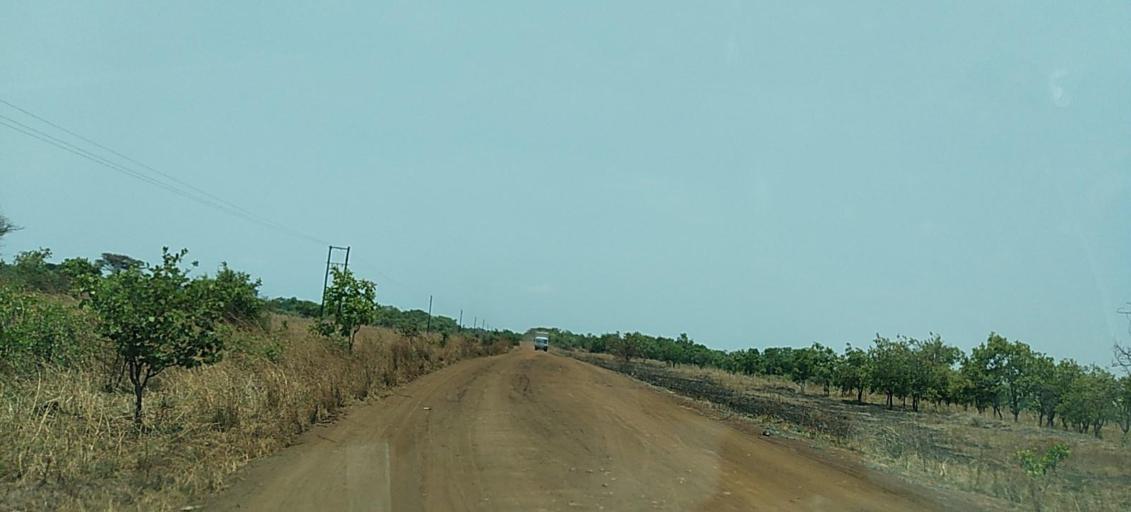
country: ZM
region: Copperbelt
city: Mpongwe
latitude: -13.7120
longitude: 27.8684
